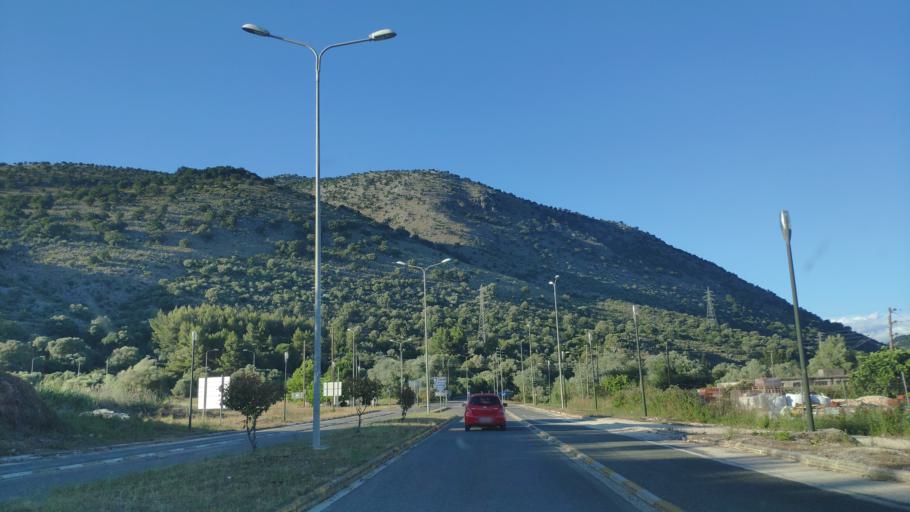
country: GR
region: Epirus
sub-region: Nomos Prevezis
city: Louros
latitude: 39.1737
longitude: 20.7635
